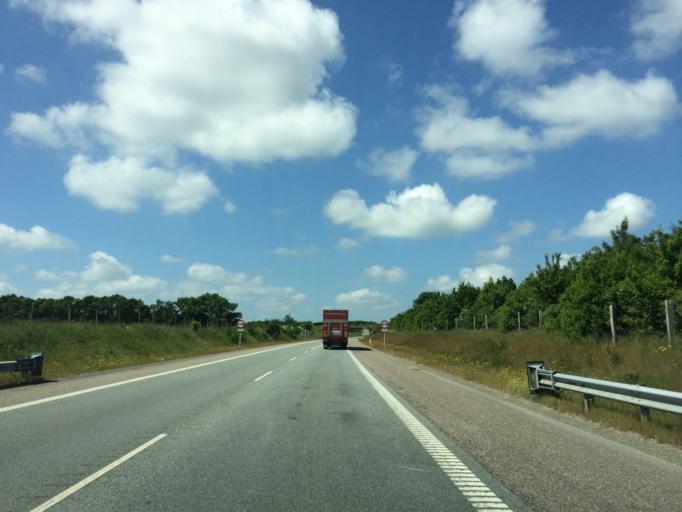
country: DK
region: Central Jutland
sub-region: Herning Kommune
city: Snejbjerg
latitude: 56.1880
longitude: 8.9174
